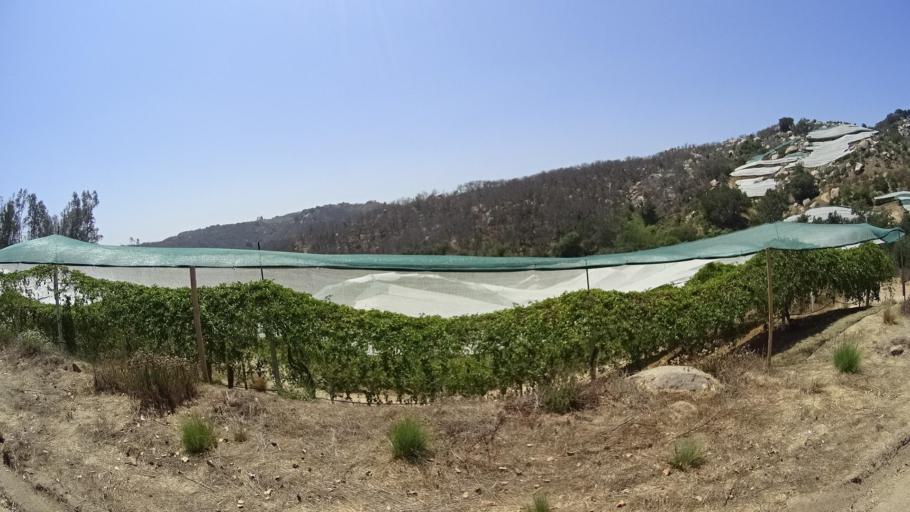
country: US
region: California
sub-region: San Diego County
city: Fallbrook
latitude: 33.4286
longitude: -117.2625
